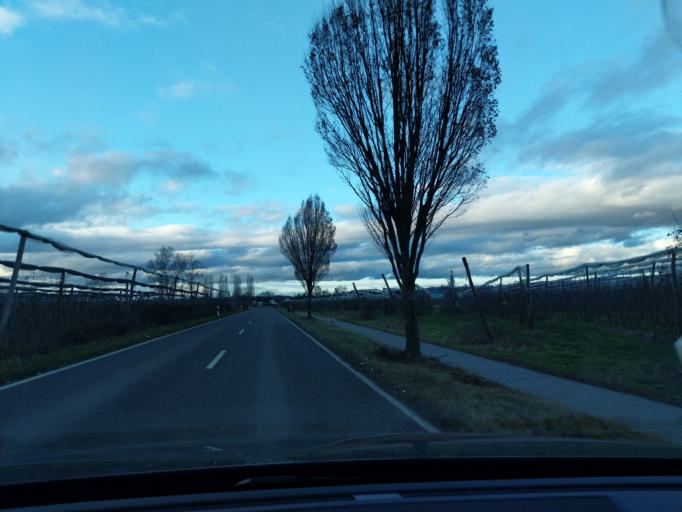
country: DE
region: Baden-Wuerttemberg
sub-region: Tuebingen Region
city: Bermatingen
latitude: 47.7183
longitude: 9.3290
